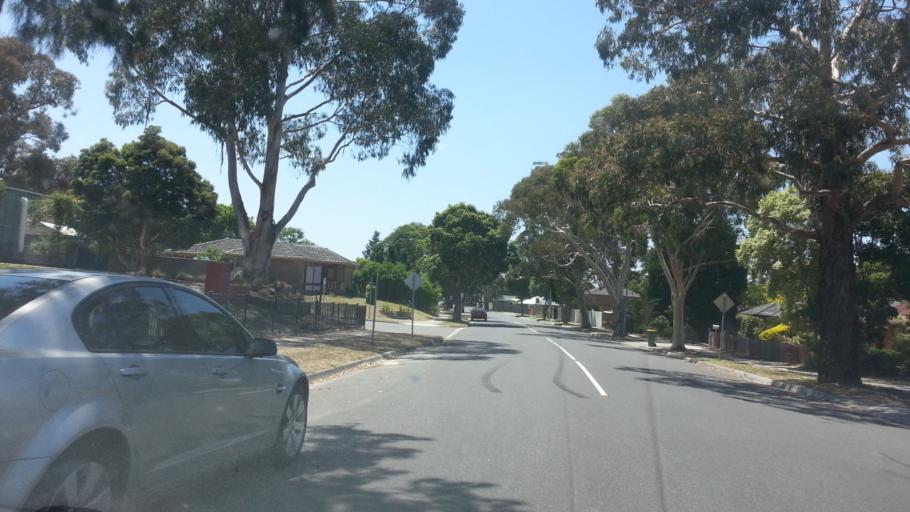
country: AU
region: Victoria
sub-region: Knox
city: Wantirna
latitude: -37.8549
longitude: 145.2366
